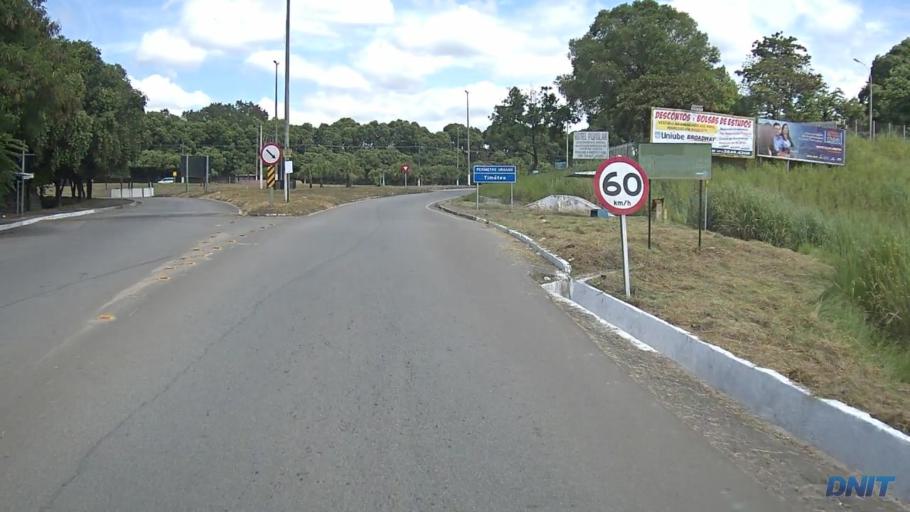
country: BR
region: Minas Gerais
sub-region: Coronel Fabriciano
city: Coronel Fabriciano
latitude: -19.5262
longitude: -42.6404
